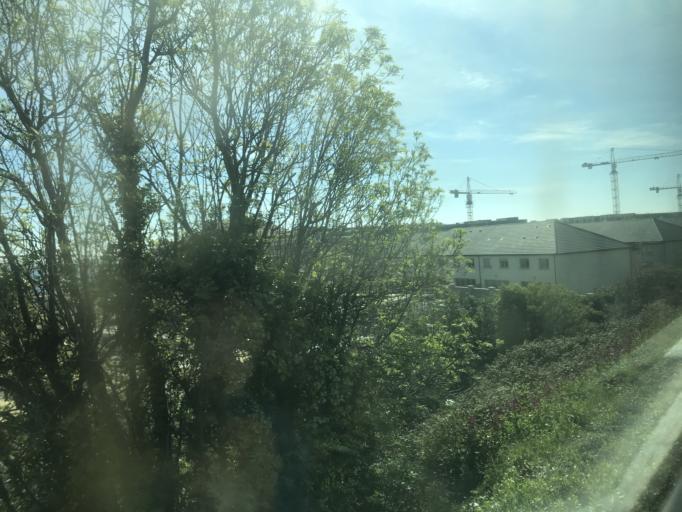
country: IE
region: Leinster
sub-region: Wicklow
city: Greystones
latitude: 53.1537
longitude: -6.0718
